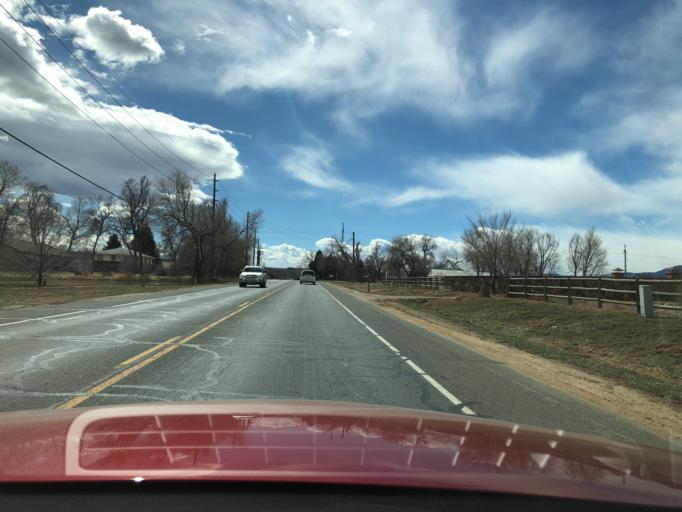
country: US
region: Colorado
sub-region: Boulder County
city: Gunbarrel
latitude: 40.0204
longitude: -105.1784
